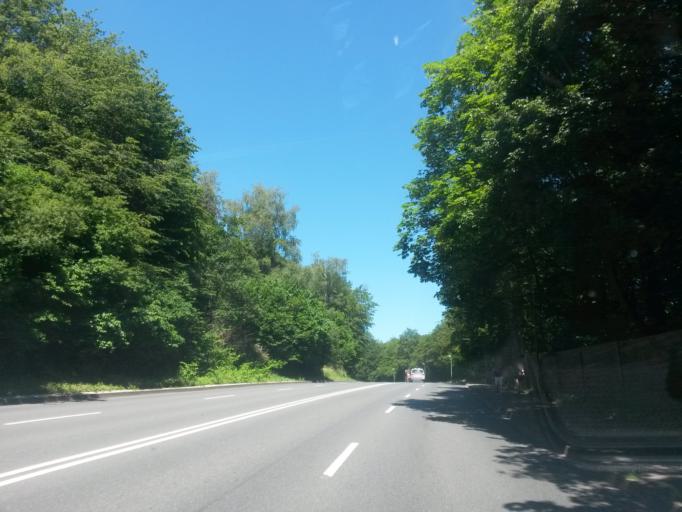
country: DE
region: North Rhine-Westphalia
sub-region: Regierungsbezirk Arnsberg
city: Luedenscheid
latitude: 51.2291
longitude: 7.6316
